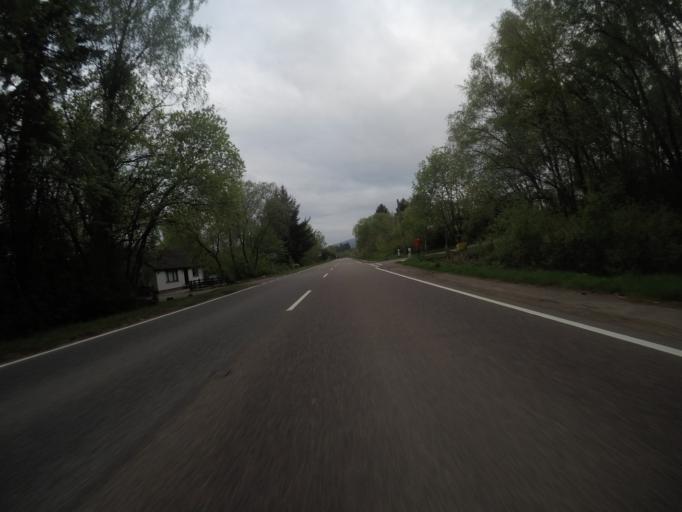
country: GB
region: Scotland
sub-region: Highland
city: Spean Bridge
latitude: 56.8900
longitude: -4.8644
